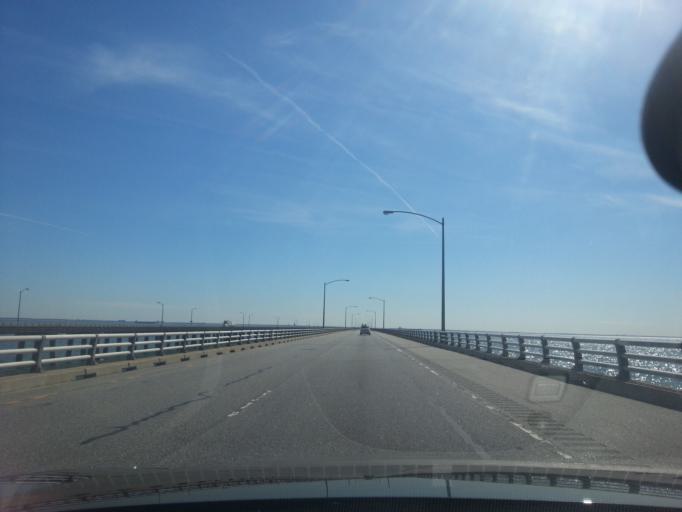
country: US
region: Virginia
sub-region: City of Virginia Beach
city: Virginia Beach
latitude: 37.0196
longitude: -76.0916
